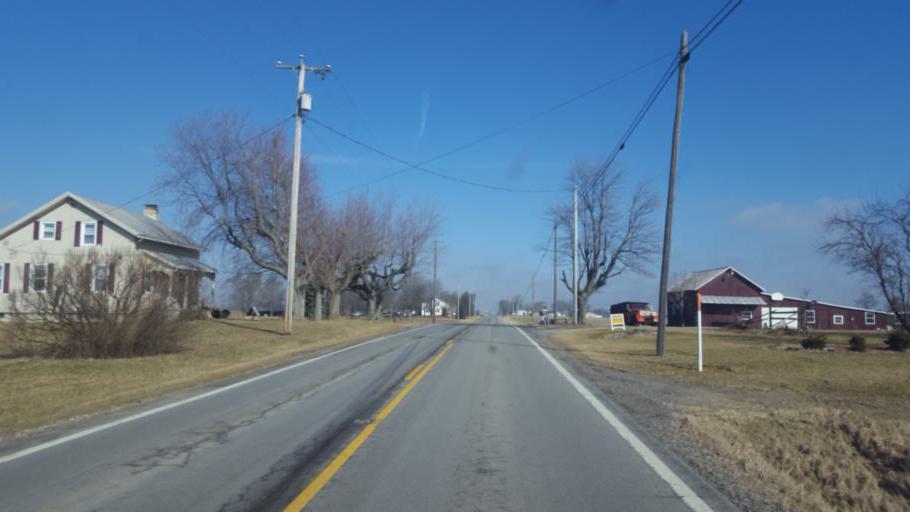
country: US
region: Ohio
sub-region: Crawford County
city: Bucyrus
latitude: 40.8696
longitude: -82.9633
